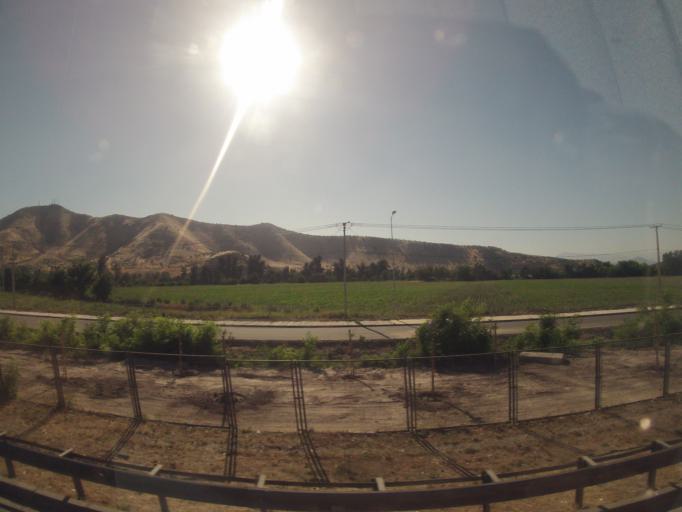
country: CL
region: Santiago Metropolitan
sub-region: Provincia de Maipo
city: San Bernardo
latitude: -33.5844
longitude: -70.7142
